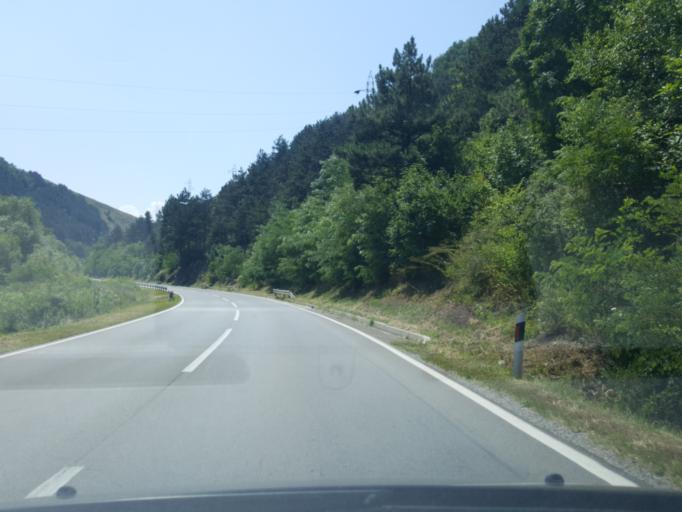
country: RS
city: Prislonica
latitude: 43.9933
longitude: 20.4216
